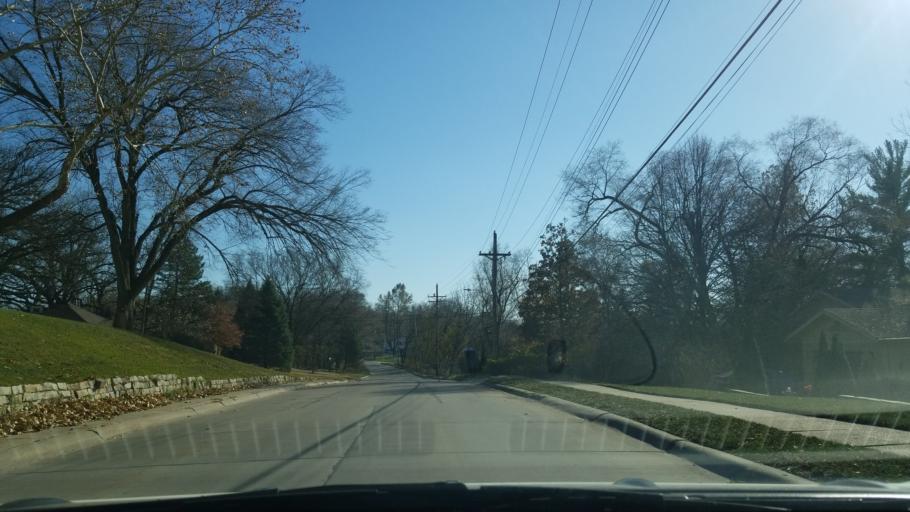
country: US
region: Nebraska
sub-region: Sarpy County
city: Bellevue
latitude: 41.1566
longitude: -95.9014
